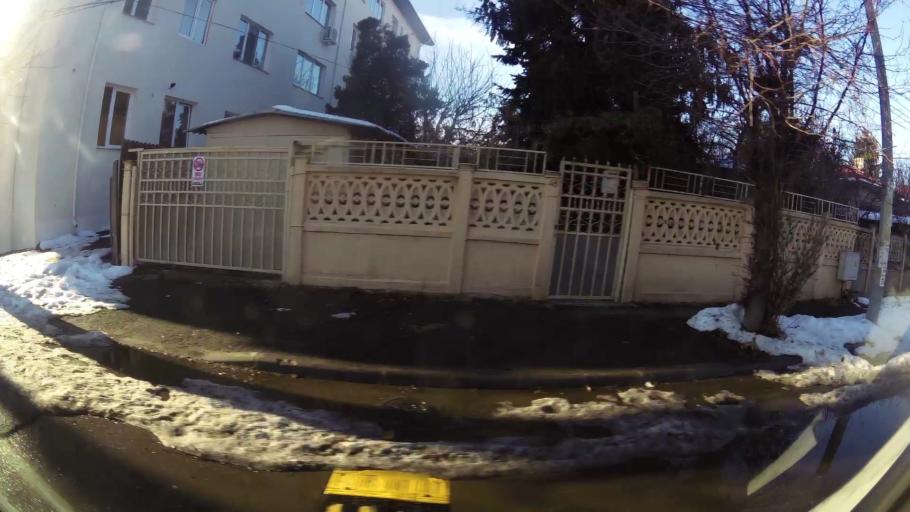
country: RO
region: Bucuresti
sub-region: Municipiul Bucuresti
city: Bucuresti
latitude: 44.3911
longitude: 26.0909
